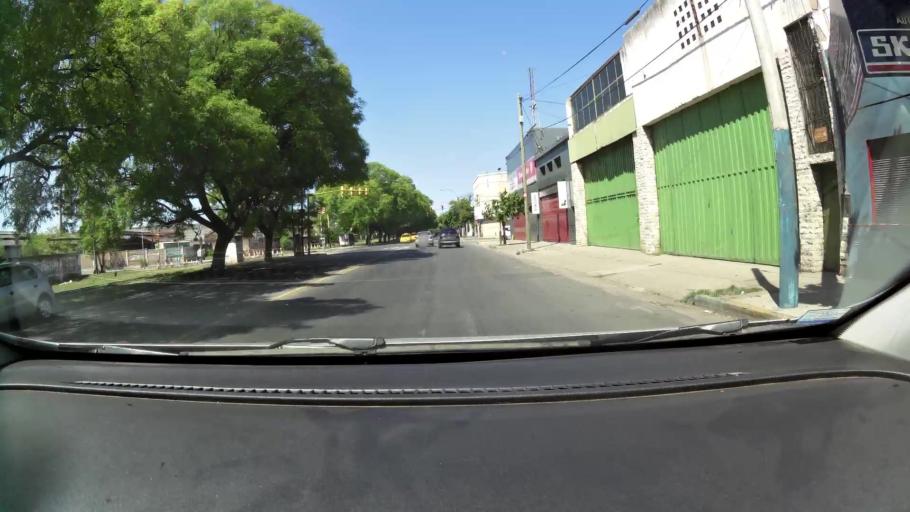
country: AR
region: Cordoba
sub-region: Departamento de Capital
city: Cordoba
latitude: -31.3970
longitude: -64.1626
